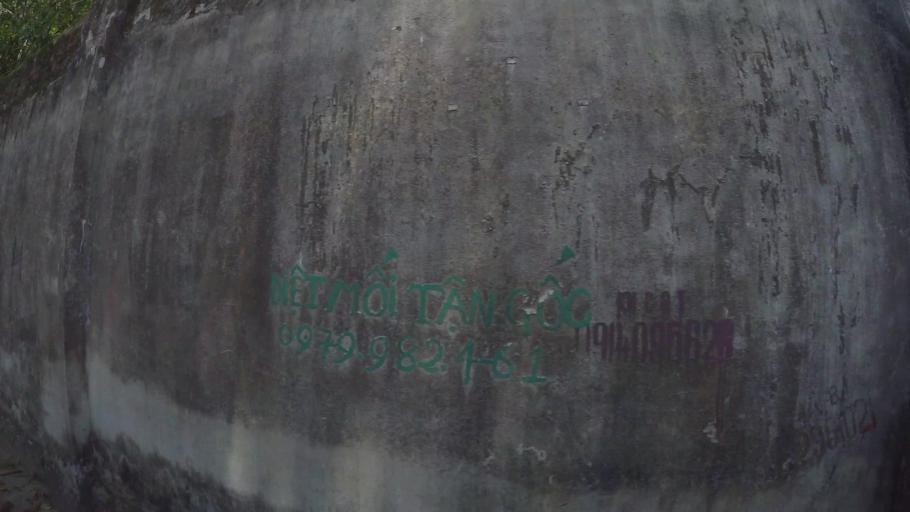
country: VN
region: Ha Noi
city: Van Dien
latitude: 20.9539
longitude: 105.8237
